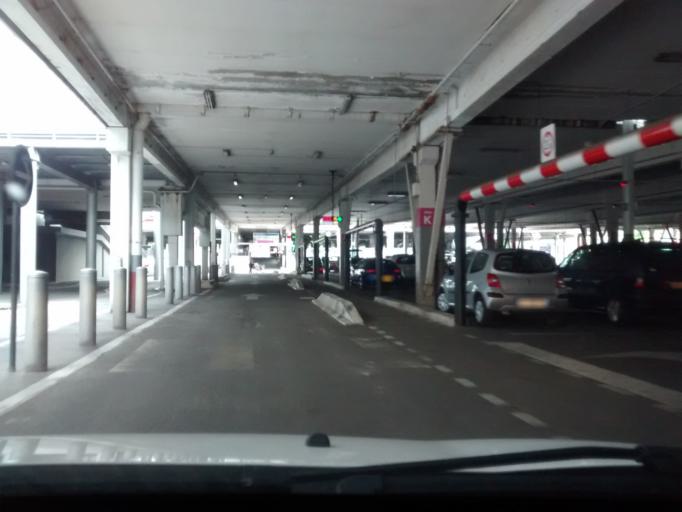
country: FR
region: Ile-de-France
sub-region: Departement de l'Essonne
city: Bievres
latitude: 48.7799
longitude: 2.2184
